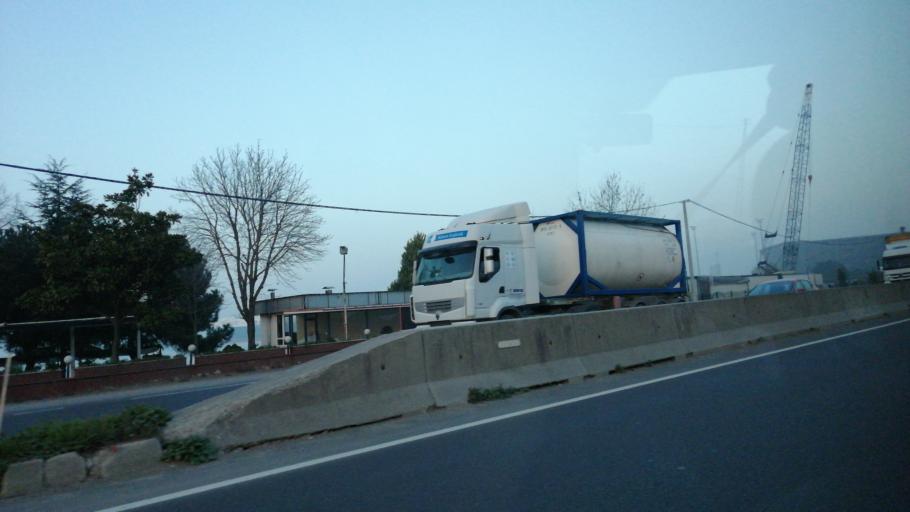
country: TR
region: Yalova
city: Taskopru
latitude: 40.6880
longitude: 29.4259
